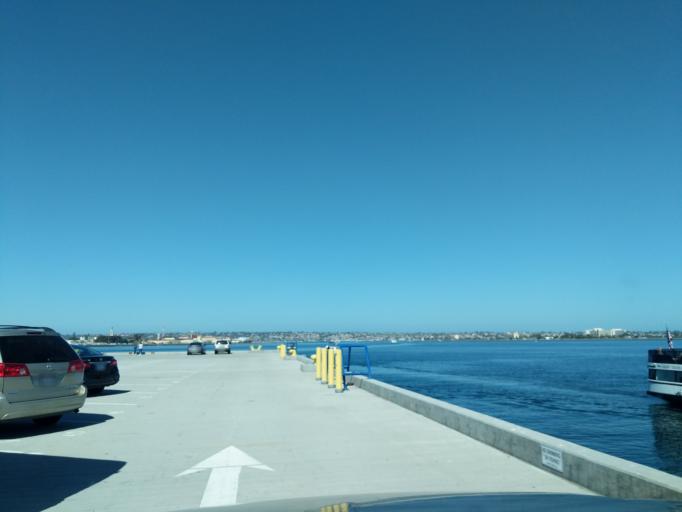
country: US
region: California
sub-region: San Diego County
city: San Diego
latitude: 32.7148
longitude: -117.1758
